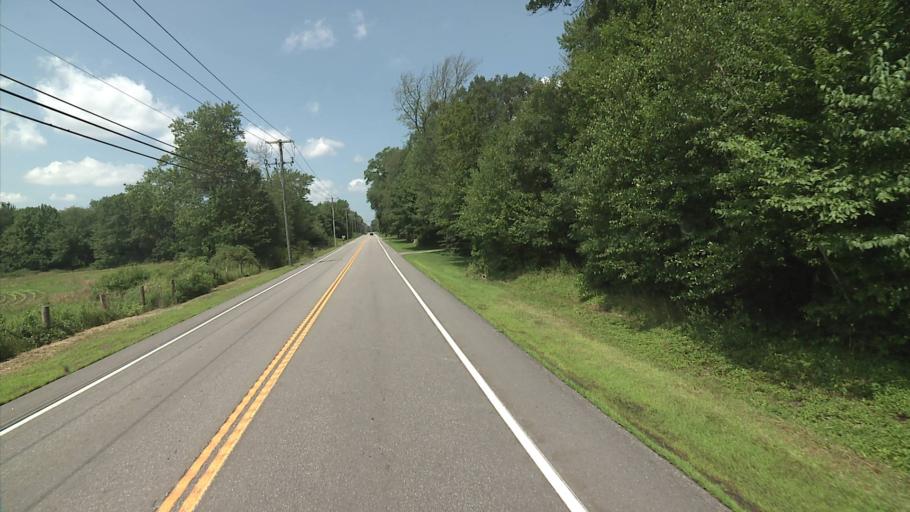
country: US
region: Connecticut
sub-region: Tolland County
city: Tolland
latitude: 41.8114
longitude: -72.3958
